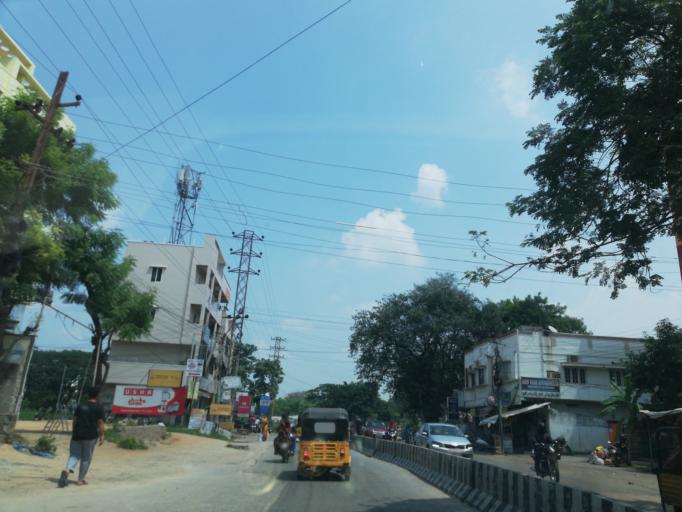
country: IN
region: Telangana
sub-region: Medak
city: Serilingampalle
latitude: 17.4830
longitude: 78.3204
